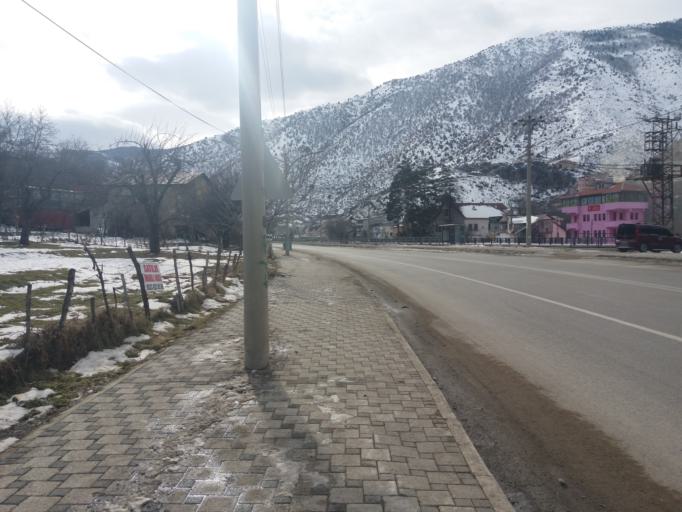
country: TR
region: Gumushane
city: Gumushkhane
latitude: 40.4433
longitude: 39.5035
